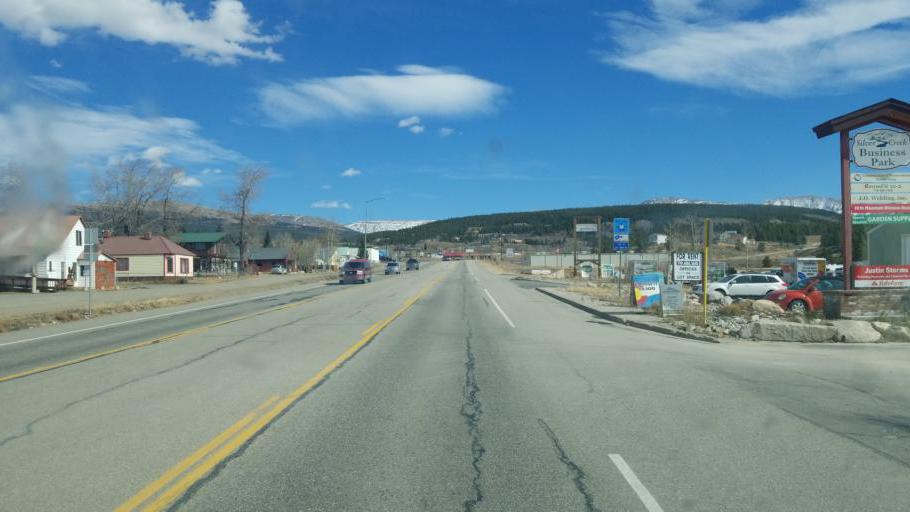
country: US
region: Colorado
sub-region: Lake County
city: Leadville
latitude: 39.2408
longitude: -106.2993
